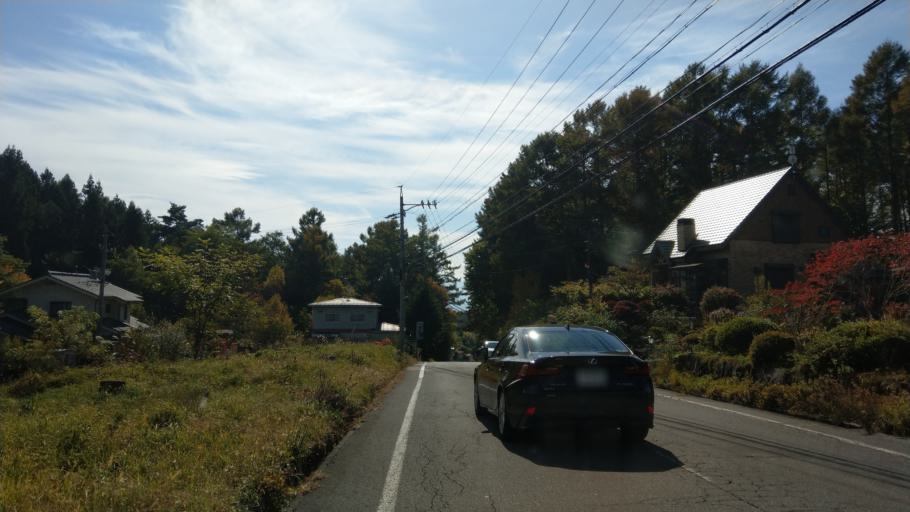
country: JP
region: Nagano
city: Komoro
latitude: 36.3490
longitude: 138.4460
